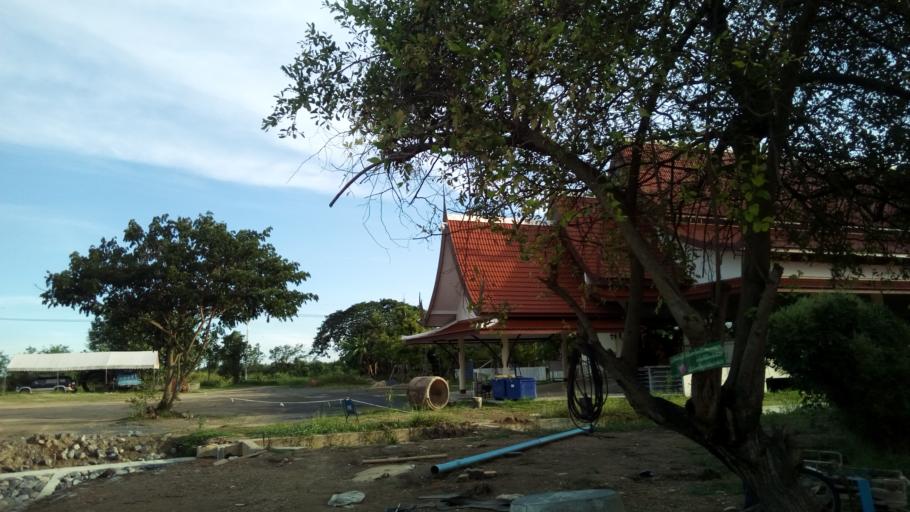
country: TH
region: Pathum Thani
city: Ban Lam Luk Ka
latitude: 13.9976
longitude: 100.8357
